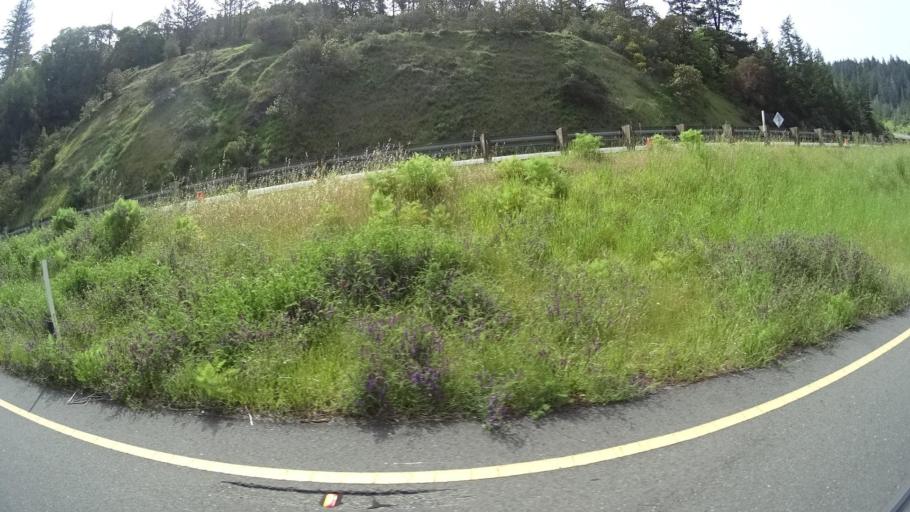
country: US
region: California
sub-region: Humboldt County
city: Redway
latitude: 40.1434
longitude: -123.8069
